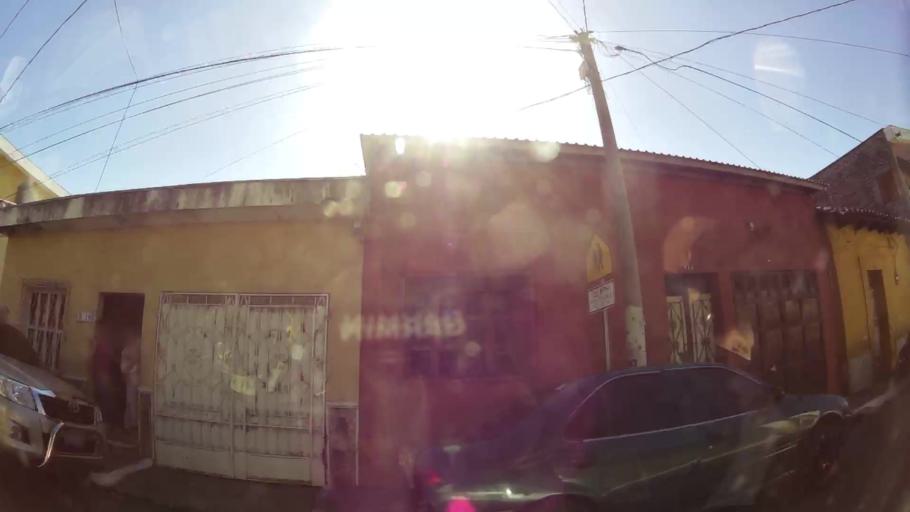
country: SV
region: Sonsonate
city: Sonsonate
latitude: 13.7261
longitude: -89.7236
